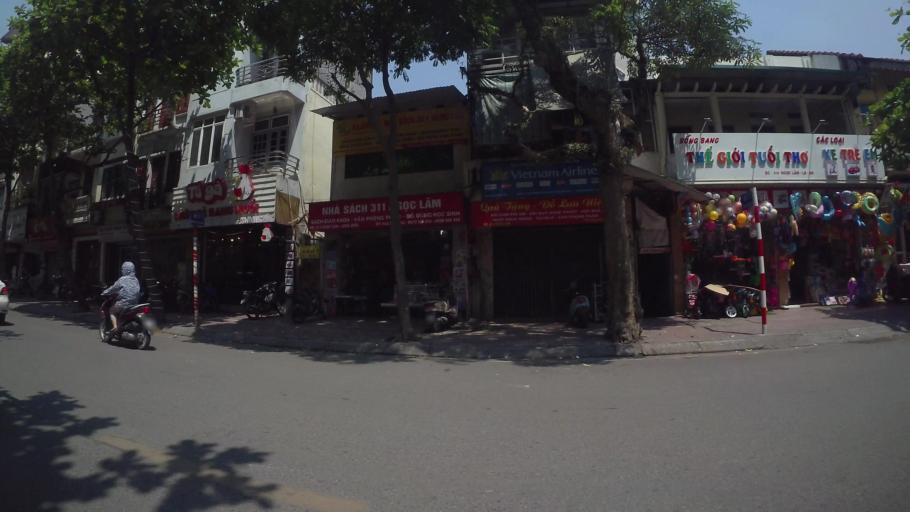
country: VN
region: Ha Noi
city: Hoan Kiem
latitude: 21.0472
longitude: 105.8725
